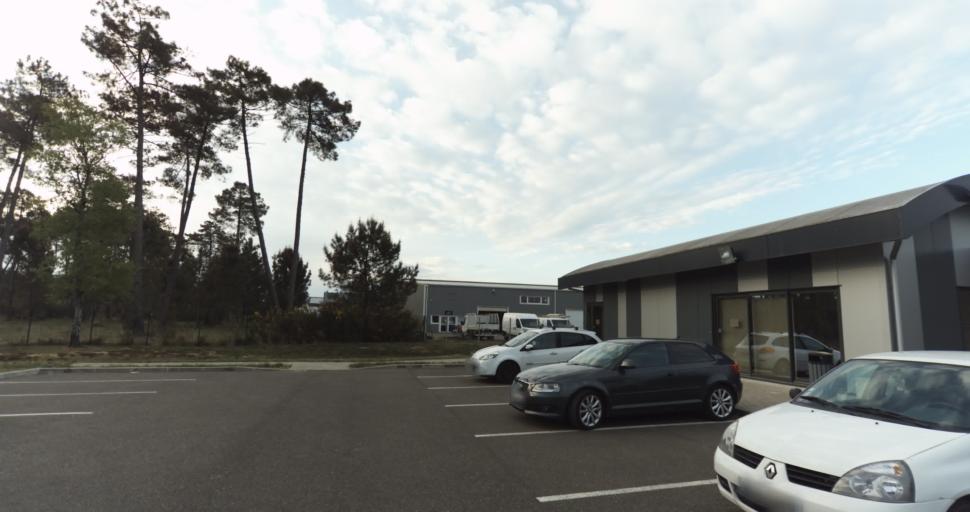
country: FR
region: Aquitaine
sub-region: Departement de la Gironde
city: Martignas-sur-Jalle
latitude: 44.7861
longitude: -0.7775
